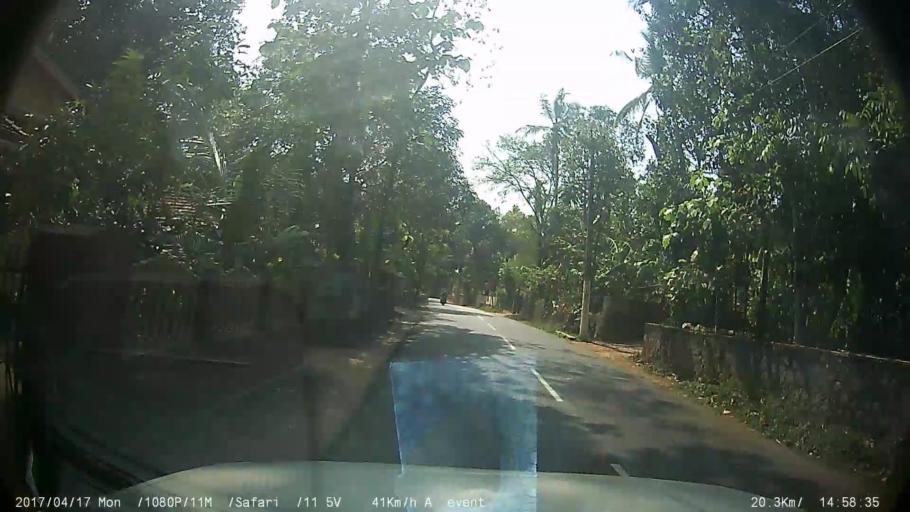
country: IN
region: Kerala
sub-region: Ernakulam
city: Piravam
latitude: 9.8359
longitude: 76.4980
